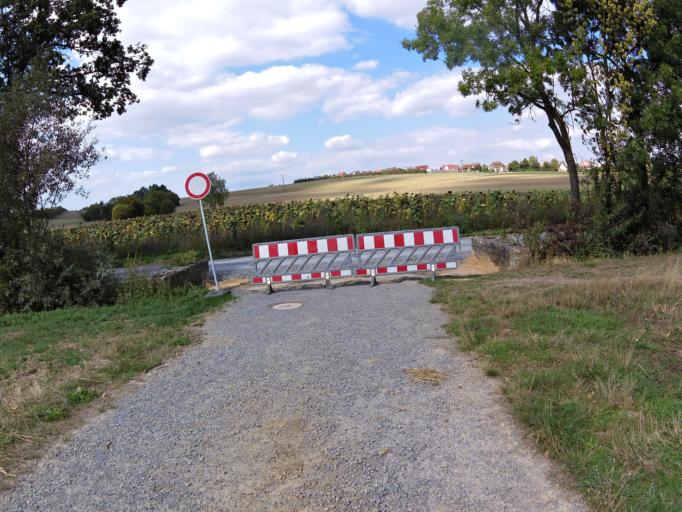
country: DE
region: Bavaria
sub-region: Regierungsbezirk Unterfranken
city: Hettstadt
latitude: 49.7944
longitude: 9.8138
